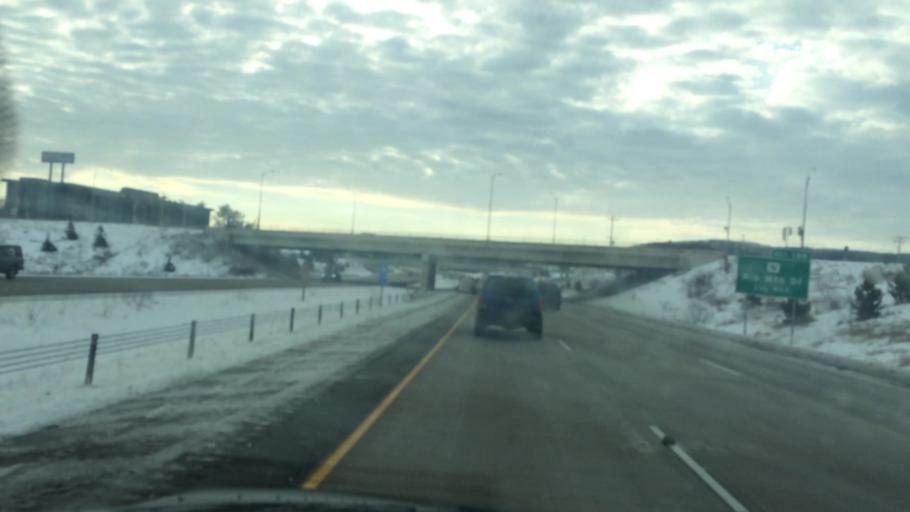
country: US
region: Wisconsin
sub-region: Marathon County
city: Rib Mountain
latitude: 44.9343
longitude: -89.6652
